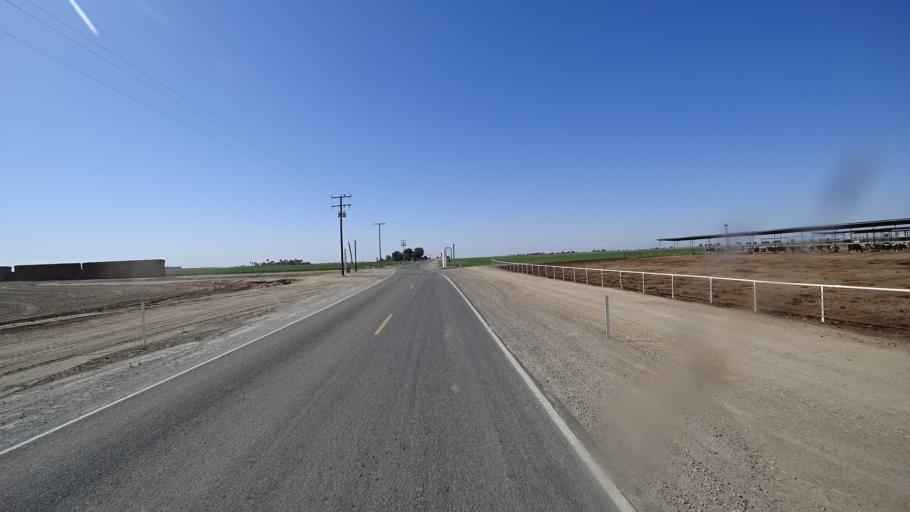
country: US
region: California
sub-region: Kings County
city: Home Garden
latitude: 36.2414
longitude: -119.5473
